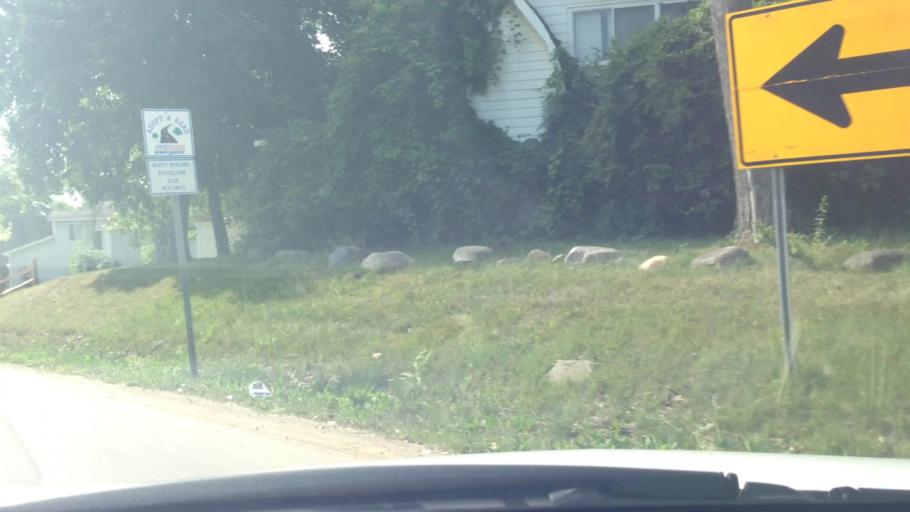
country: US
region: Michigan
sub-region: Oakland County
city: Waterford
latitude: 42.6923
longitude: -83.4414
